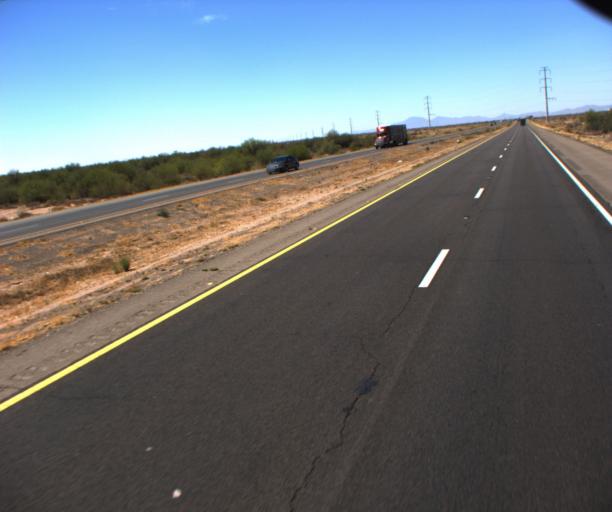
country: US
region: Arizona
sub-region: Pinal County
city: Maricopa
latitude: 33.1359
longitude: -112.0112
